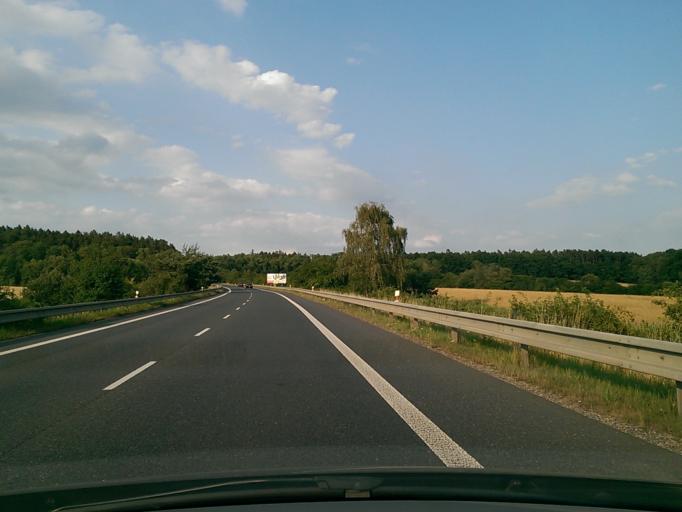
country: CZ
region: Central Bohemia
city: Dolni Bousov
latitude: 50.4492
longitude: 15.0798
